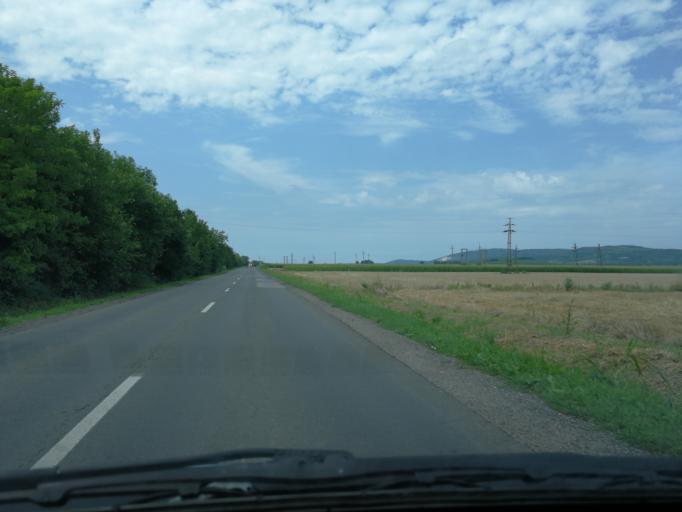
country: HU
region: Baranya
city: Siklos
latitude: 45.8495
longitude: 18.3553
